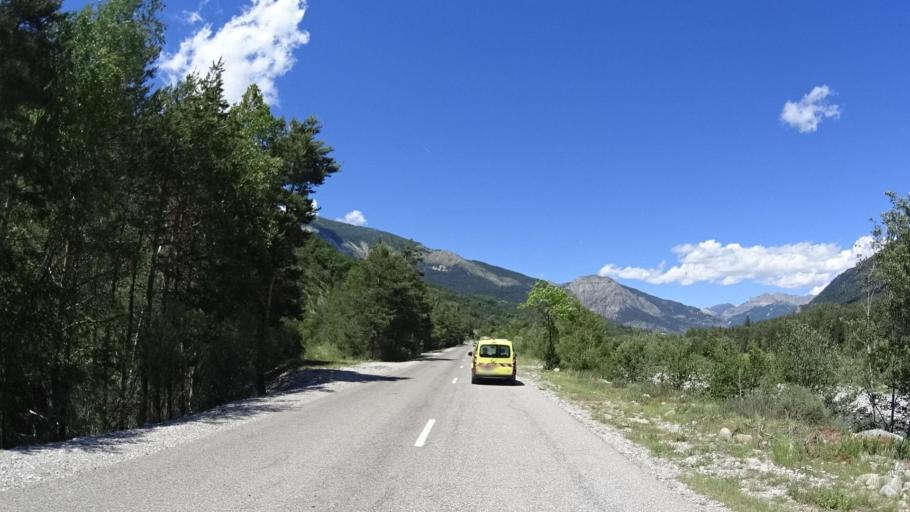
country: FR
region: Provence-Alpes-Cote d'Azur
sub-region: Departement des Alpes-de-Haute-Provence
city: Annot
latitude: 44.1247
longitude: 6.5804
